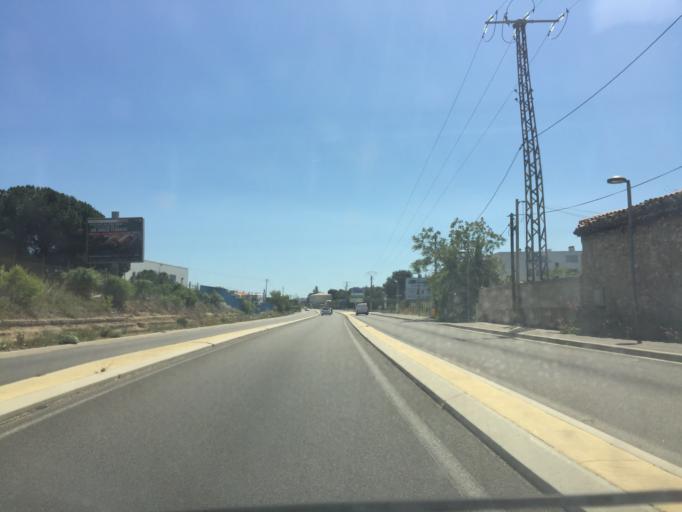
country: FR
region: Provence-Alpes-Cote d'Azur
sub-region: Departement des Bouches-du-Rhone
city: Vitrolles
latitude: 43.4644
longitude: 5.2320
